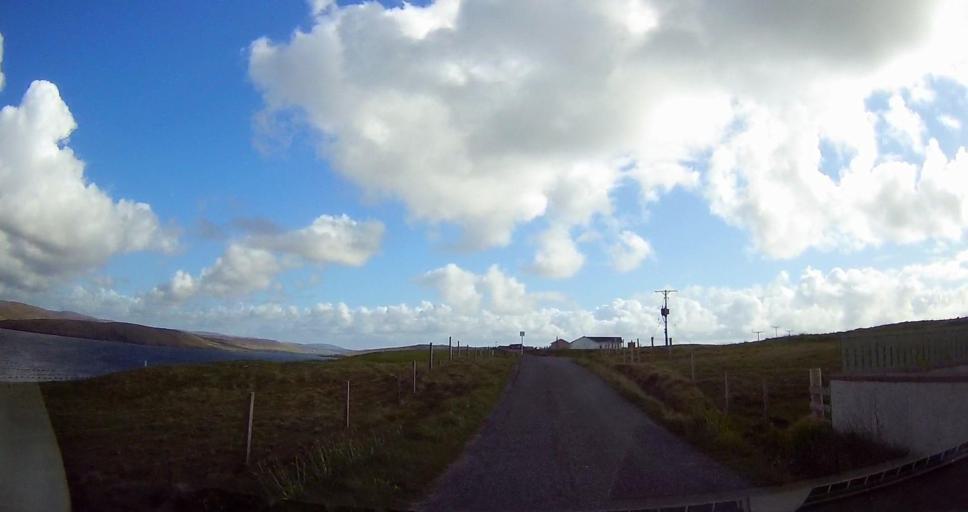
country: GB
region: Scotland
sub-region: Shetland Islands
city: Lerwick
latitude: 60.3626
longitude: -1.3826
